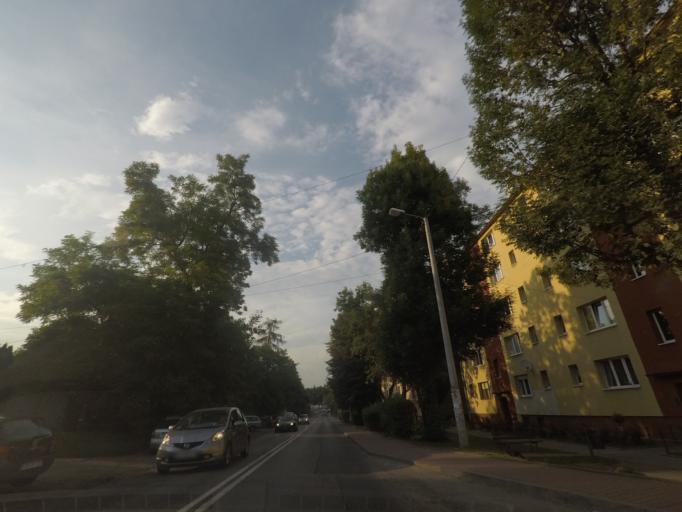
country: PL
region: Lesser Poland Voivodeship
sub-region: Powiat wielicki
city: Wieliczka
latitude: 49.9915
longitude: 20.0418
